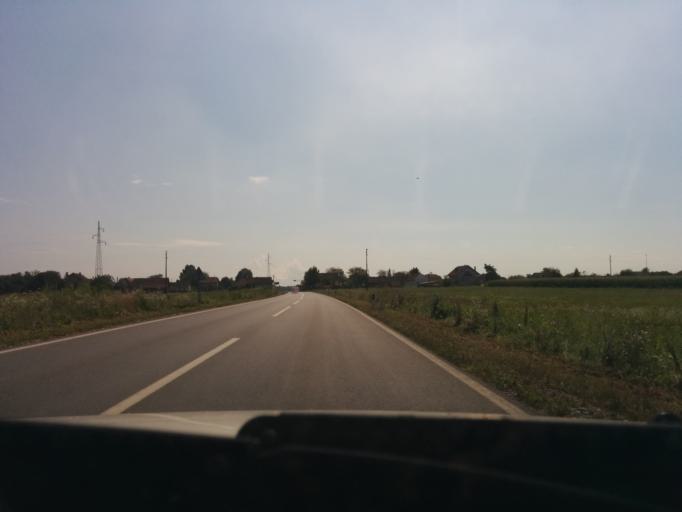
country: HR
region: Sisacko-Moslavacka
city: Husain
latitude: 45.4588
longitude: 16.8334
